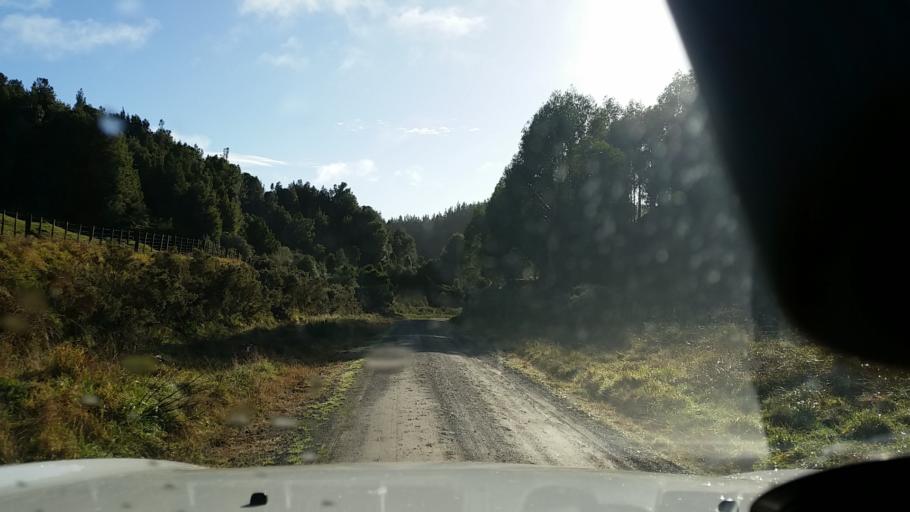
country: NZ
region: Bay of Plenty
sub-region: Kawerau District
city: Kawerau
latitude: -38.0107
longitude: 176.5974
